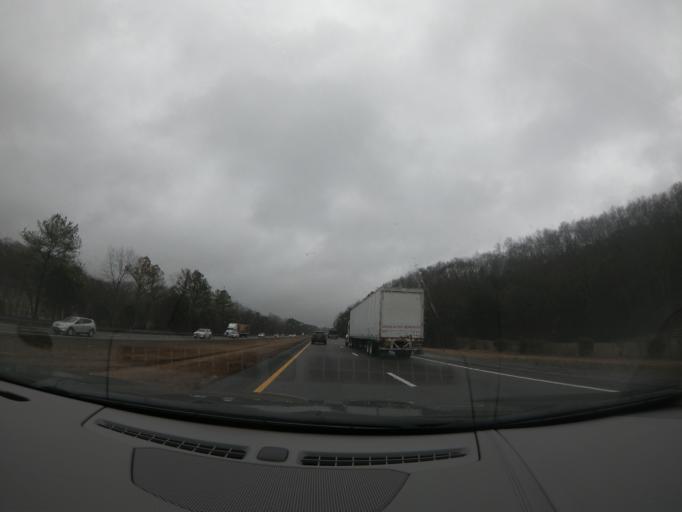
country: US
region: Tennessee
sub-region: Rutherford County
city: Plainview
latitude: 35.6382
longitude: -86.2493
